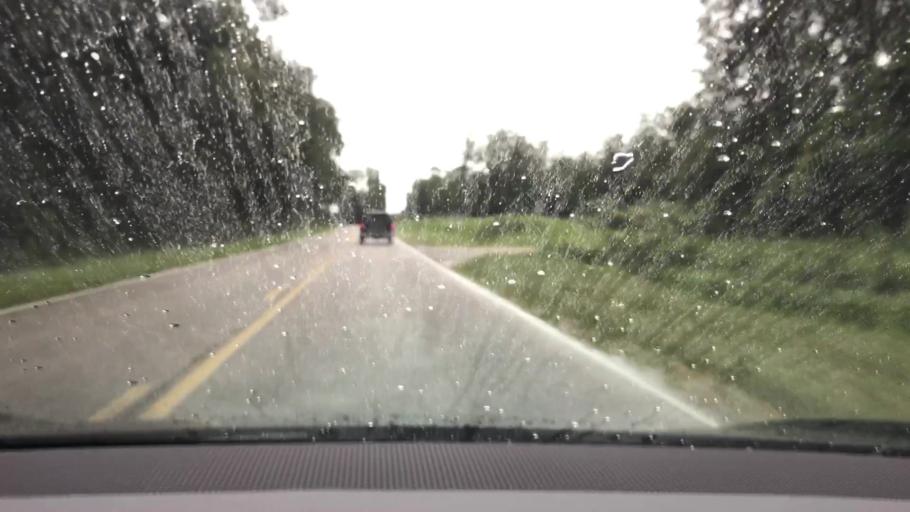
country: US
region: Alabama
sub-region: Geneva County
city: Samson
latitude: 31.1354
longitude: -86.1352
